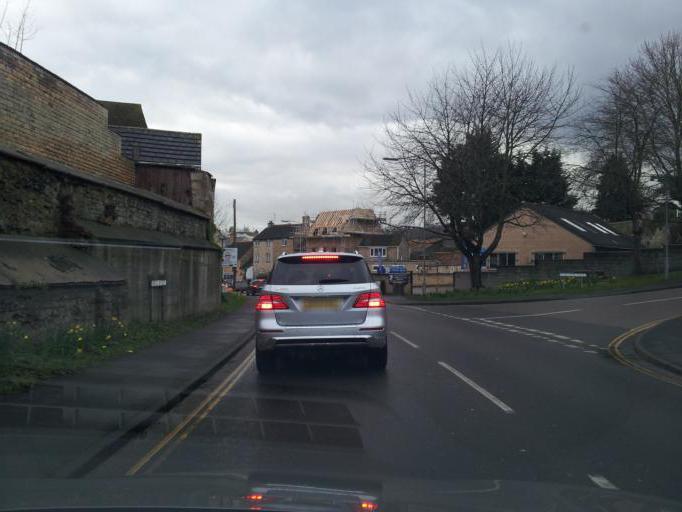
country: GB
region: England
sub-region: Lincolnshire
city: Stamford
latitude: 52.6536
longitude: -0.4826
